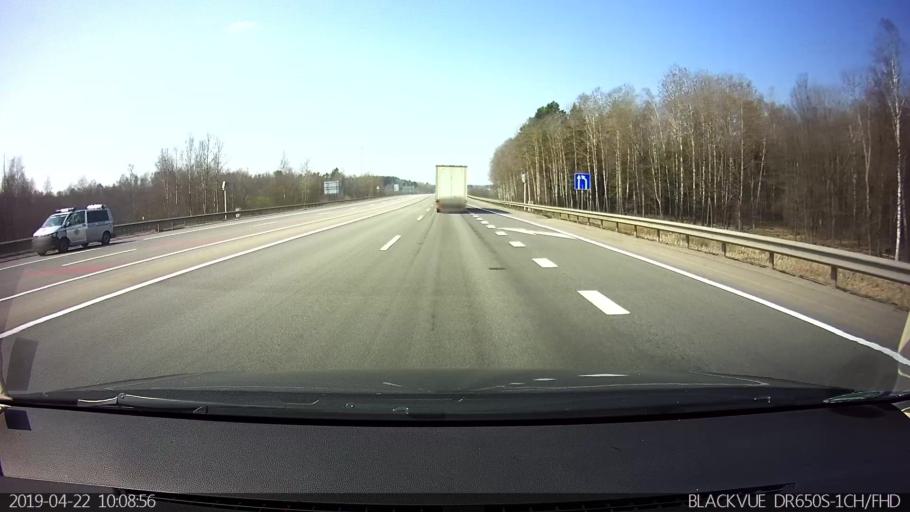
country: BY
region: Vitebsk
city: Horad Orsha
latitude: 54.6228
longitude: 30.4319
